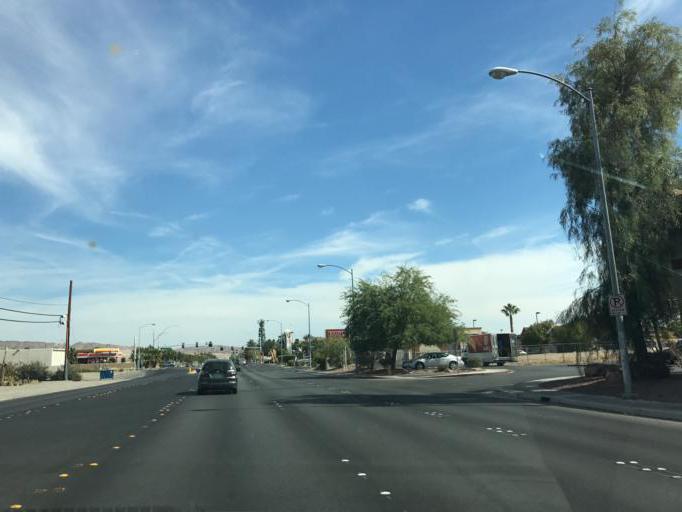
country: US
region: Nevada
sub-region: Clark County
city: Winchester
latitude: 36.1296
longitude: -115.0675
